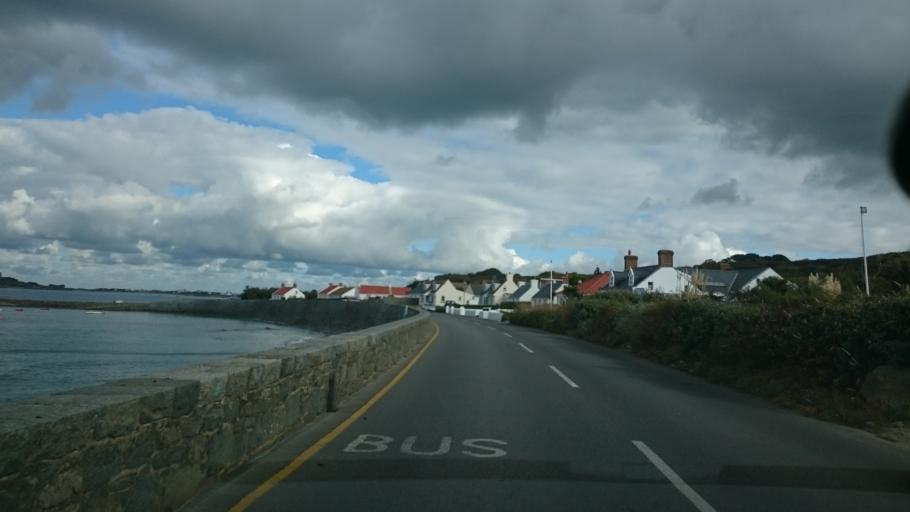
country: GG
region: St Peter Port
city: Saint Peter Port
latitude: 49.4364
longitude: -2.6543
